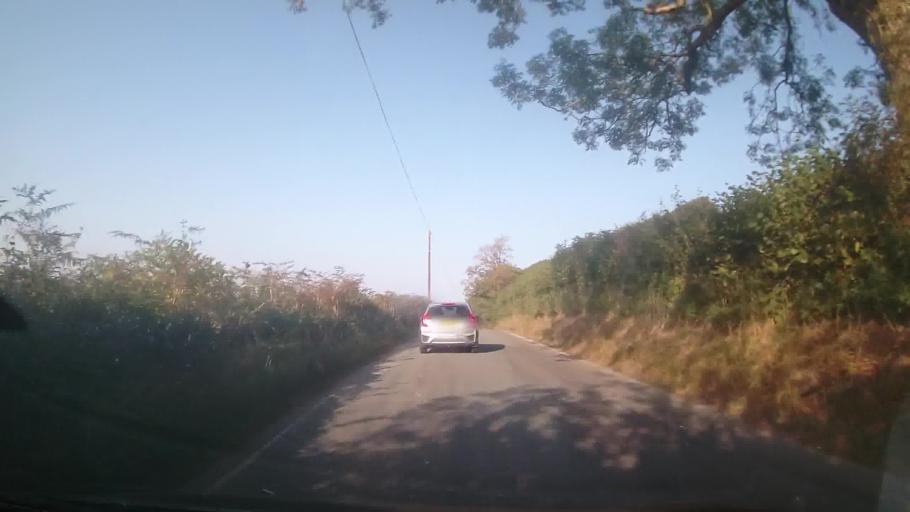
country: GB
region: Wales
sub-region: County of Ceredigion
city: Lledrod
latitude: 52.2359
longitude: -3.9283
